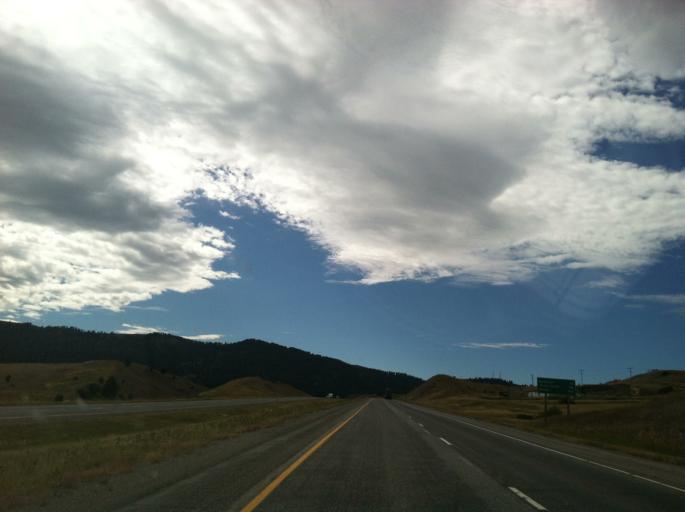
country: US
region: Montana
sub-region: Park County
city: Livingston
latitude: 45.6592
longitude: -110.7582
